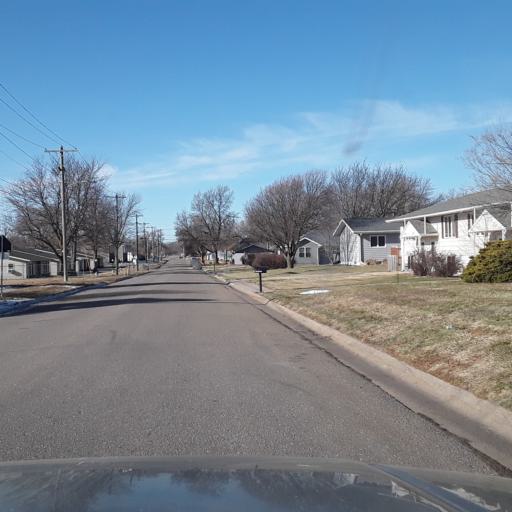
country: US
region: Nebraska
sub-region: Adams County
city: Hastings
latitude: 40.5771
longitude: -98.3986
